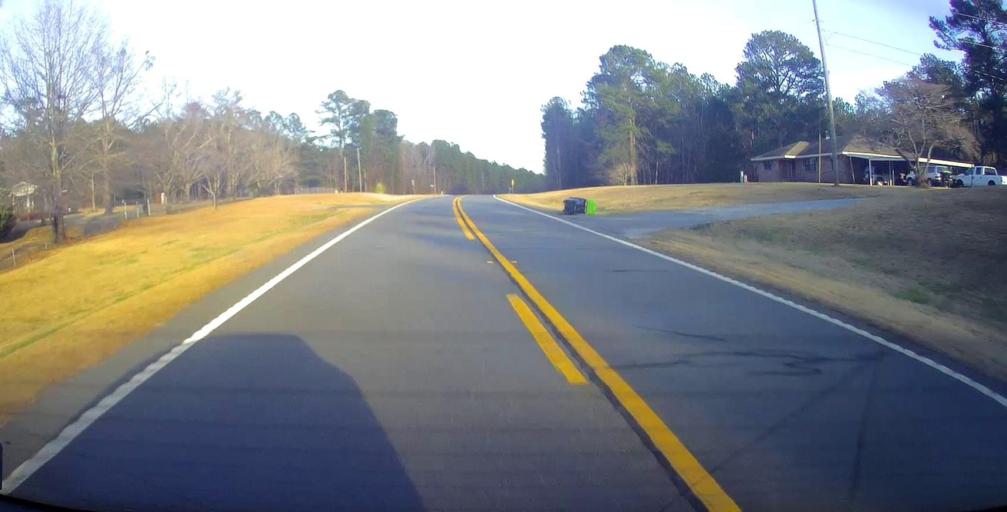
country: US
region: Georgia
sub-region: Talbot County
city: Sardis
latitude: 32.7924
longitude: -84.5435
